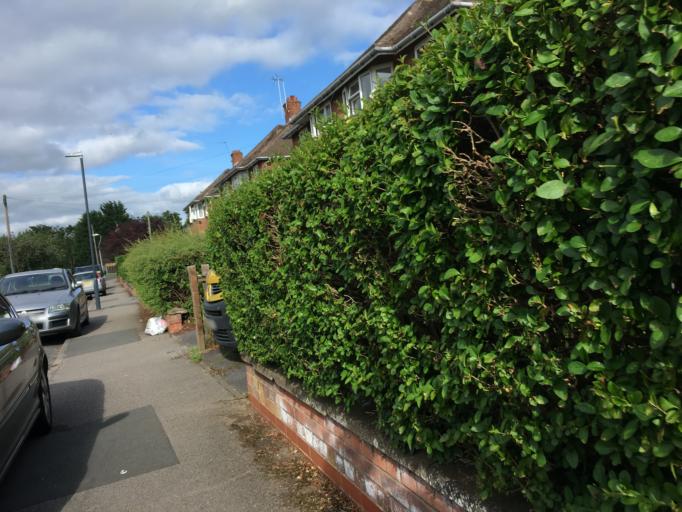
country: GB
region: England
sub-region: Warwickshire
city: Rugby
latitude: 52.3633
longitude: -1.2645
